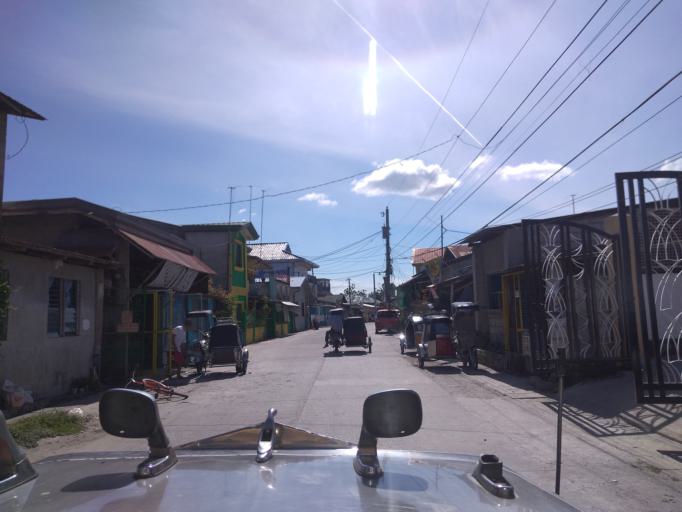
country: PH
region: Central Luzon
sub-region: Province of Pampanga
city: San Agustin
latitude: 14.9905
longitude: 120.6032
